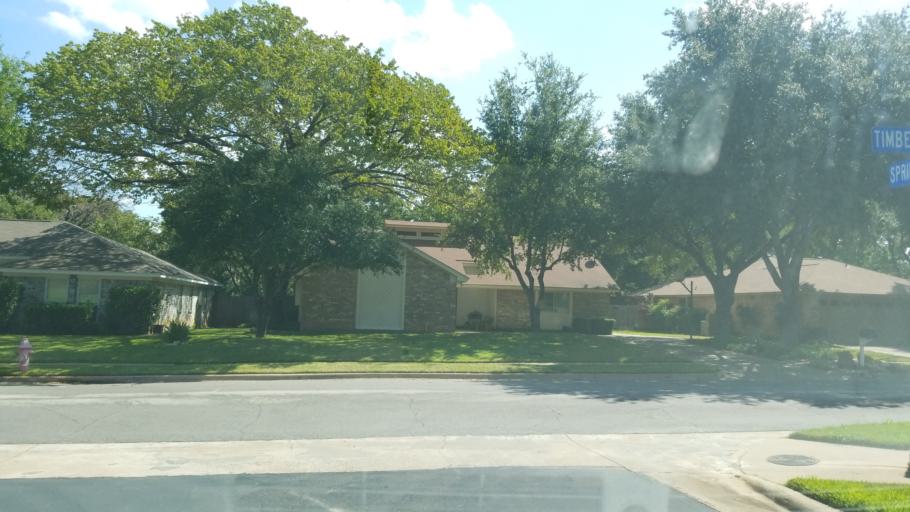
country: US
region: Texas
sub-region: Tarrant County
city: Euless
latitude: 32.8547
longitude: -97.0973
